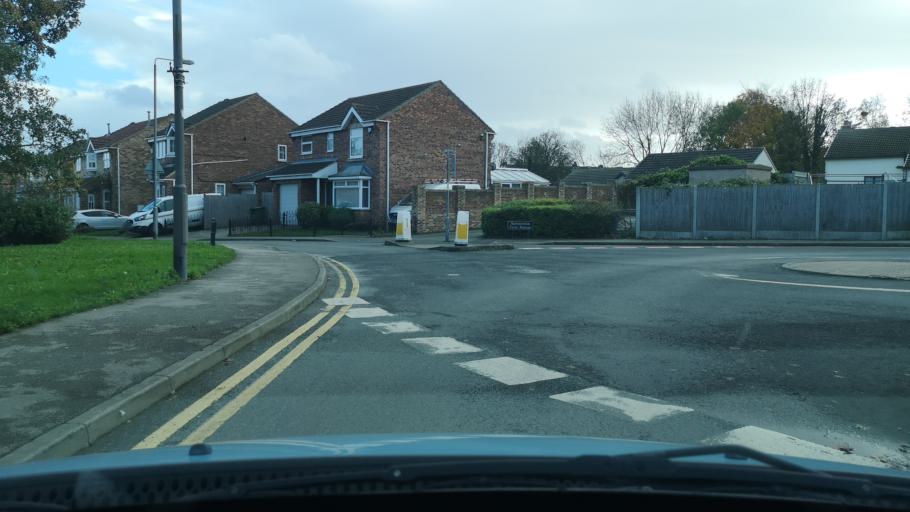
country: GB
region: England
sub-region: City and Borough of Wakefield
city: Ryhill
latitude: 53.6242
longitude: -1.4169
